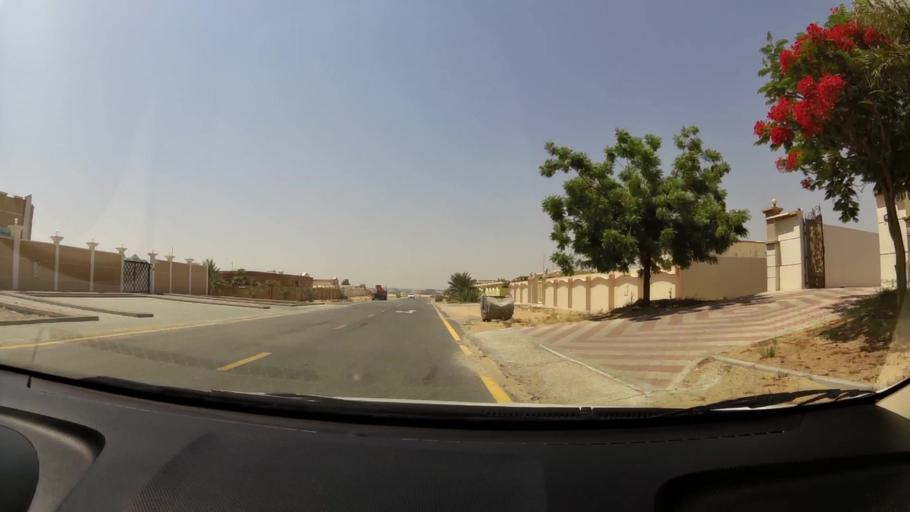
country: AE
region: Umm al Qaywayn
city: Umm al Qaywayn
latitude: 25.5098
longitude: 55.5866
